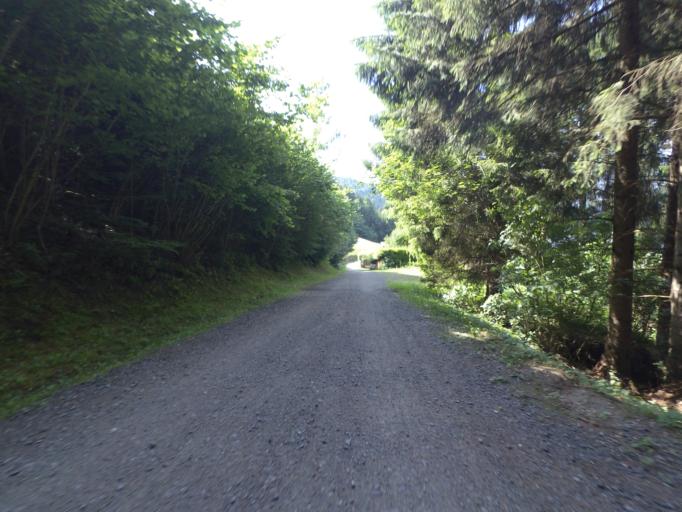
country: AT
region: Carinthia
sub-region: Politischer Bezirk Spittal an der Drau
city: Millstatt
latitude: 46.7752
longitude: 13.5994
